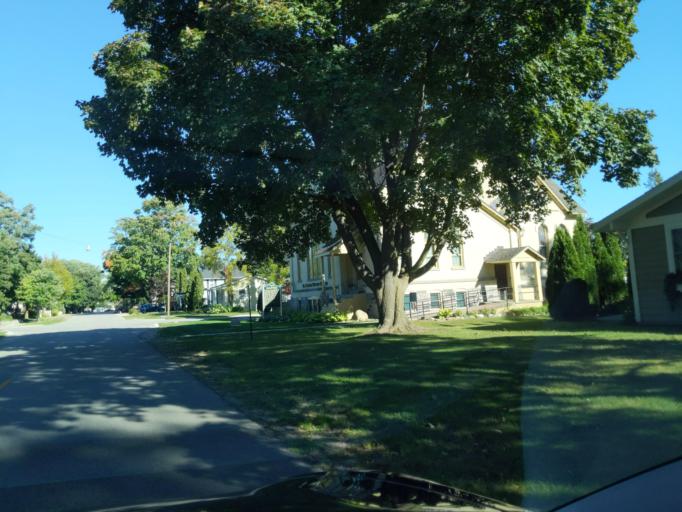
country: US
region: Michigan
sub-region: Antrim County
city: Elk Rapids
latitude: 44.8967
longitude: -85.4162
